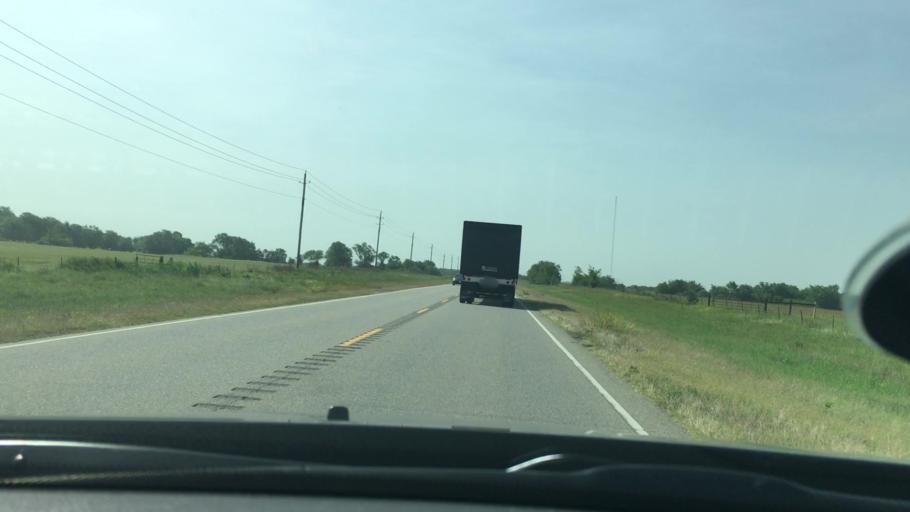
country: US
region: Oklahoma
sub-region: Atoka County
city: Atoka
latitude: 34.4294
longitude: -96.1964
